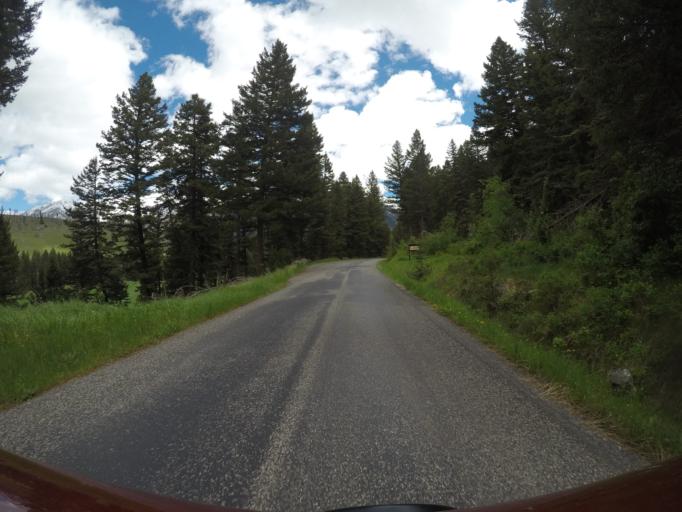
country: US
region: Montana
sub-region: Park County
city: Livingston
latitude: 45.4996
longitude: -110.5379
